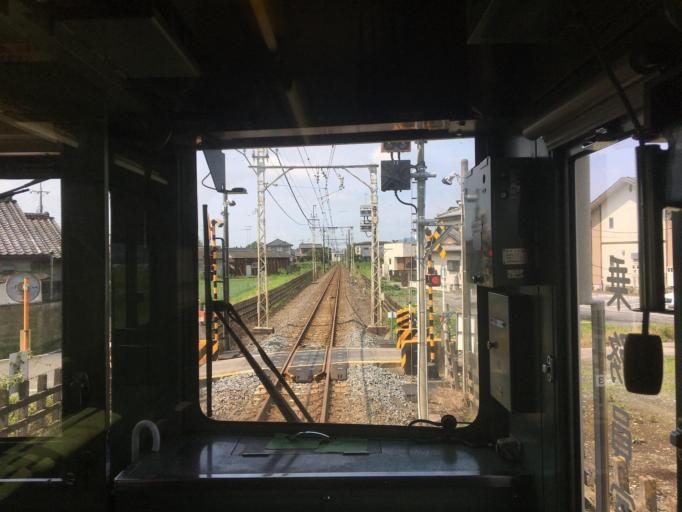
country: JP
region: Tochigi
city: Tanuma
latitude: 36.3710
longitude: 139.5859
